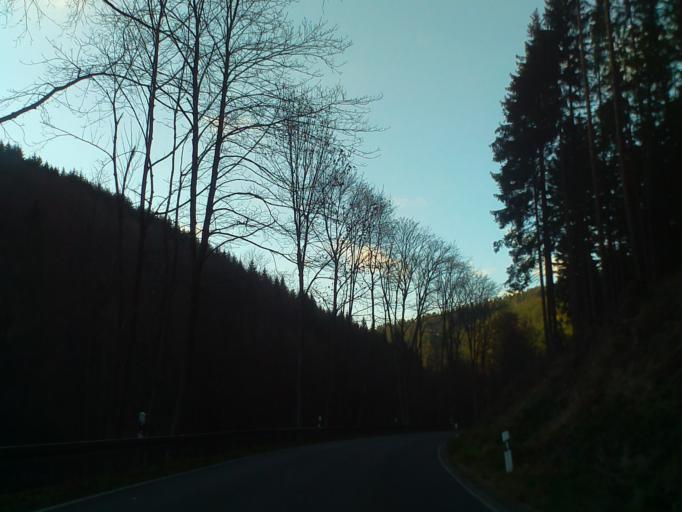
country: DE
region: Thuringia
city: Unterweissbach
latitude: 50.6120
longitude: 11.1457
